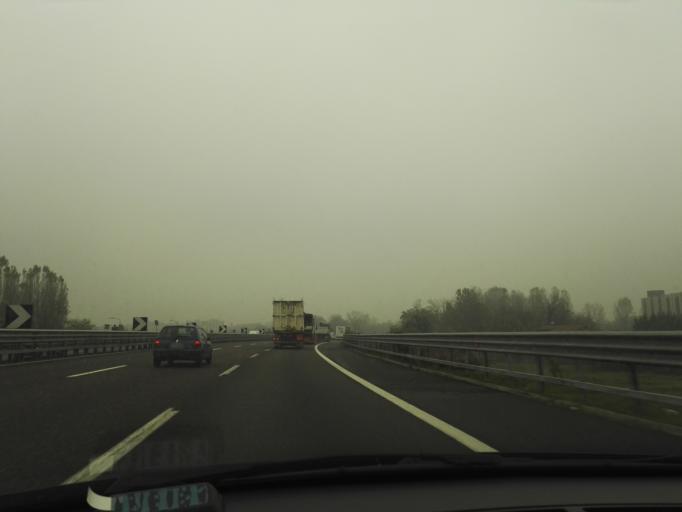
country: IT
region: Lombardy
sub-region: Citta metropolitana di Milano
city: Figino
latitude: 45.4727
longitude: 9.0796
